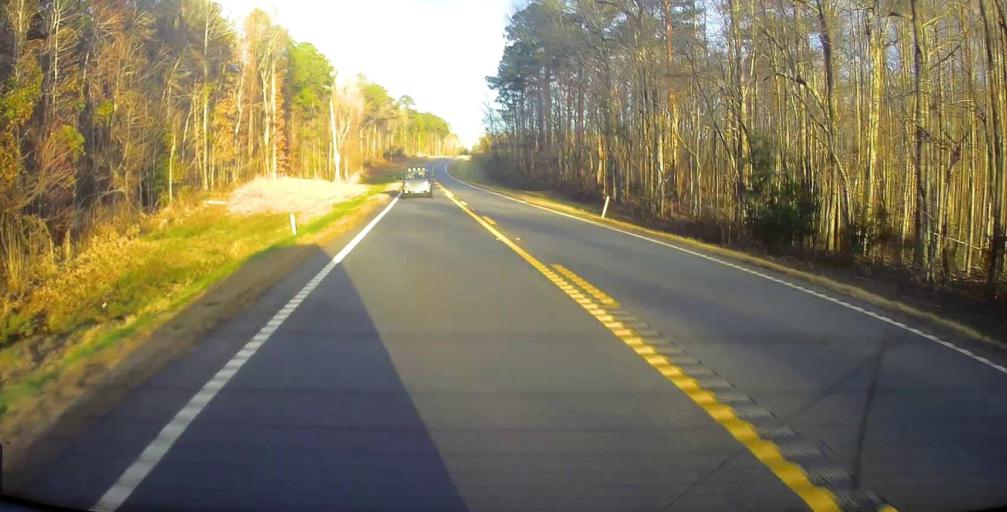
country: US
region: Georgia
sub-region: Talbot County
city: Sardis
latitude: 32.7194
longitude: -84.6724
